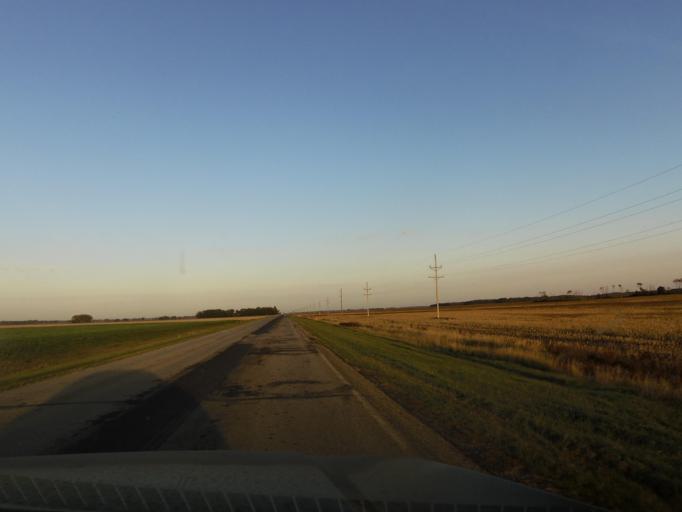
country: CA
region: Manitoba
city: Altona
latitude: 48.9635
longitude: -97.6005
